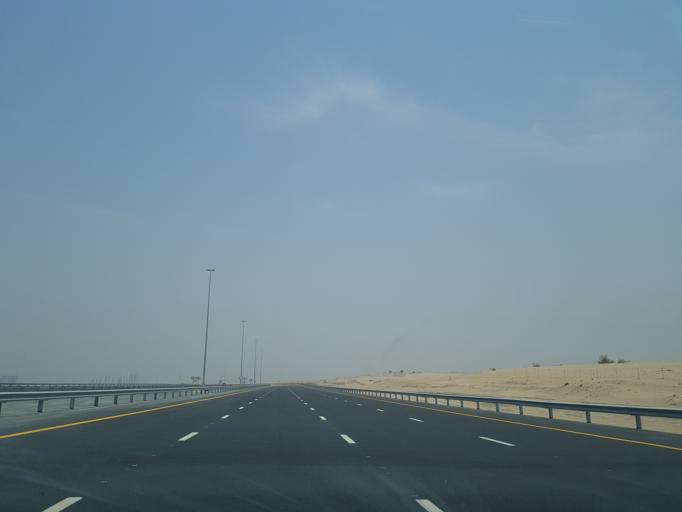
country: AE
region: Dubai
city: Dubai
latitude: 25.0105
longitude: 55.2084
